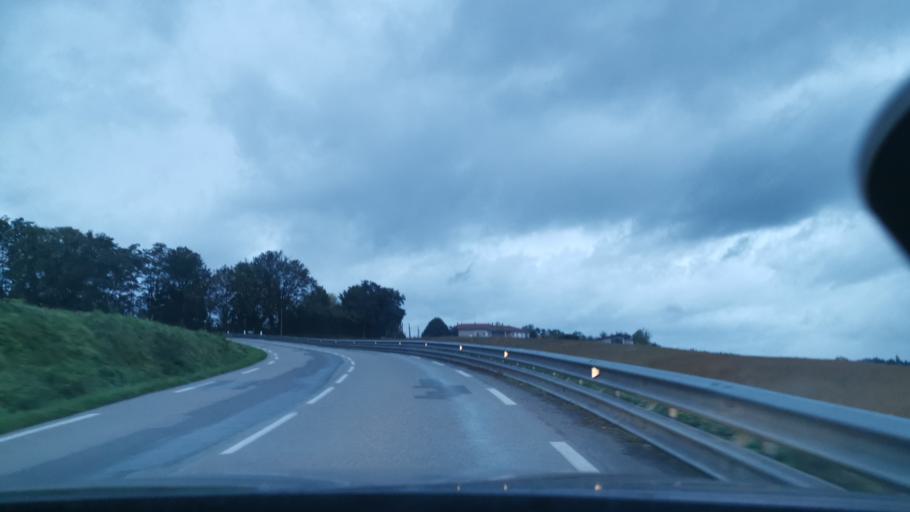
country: FR
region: Rhone-Alpes
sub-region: Departement de l'Ain
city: Vonnas
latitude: 46.1993
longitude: 4.9457
